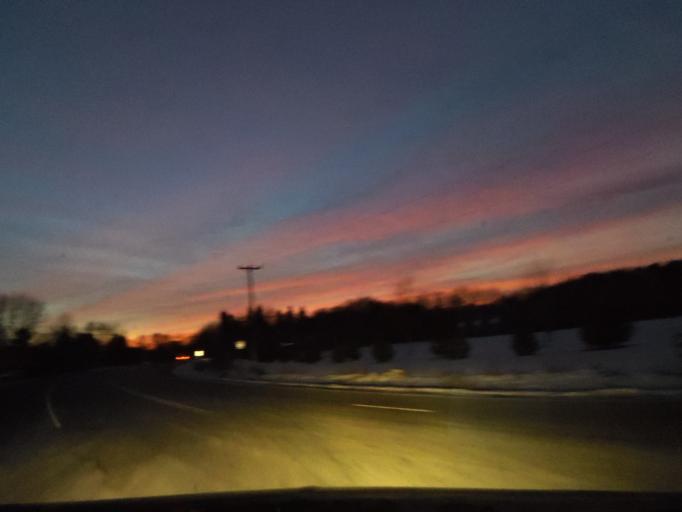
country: US
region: Minnesota
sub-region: Chisago County
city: Chisago City
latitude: 45.3468
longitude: -92.8792
